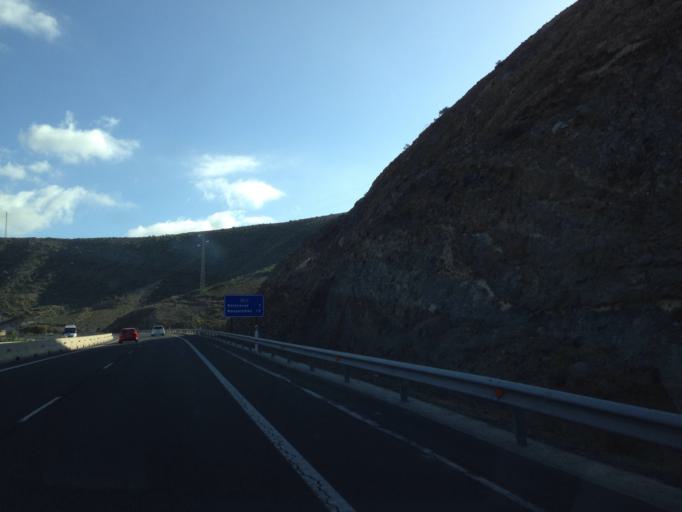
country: ES
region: Canary Islands
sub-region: Provincia de Las Palmas
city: Puerto Rico
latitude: 27.7661
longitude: -15.6665
